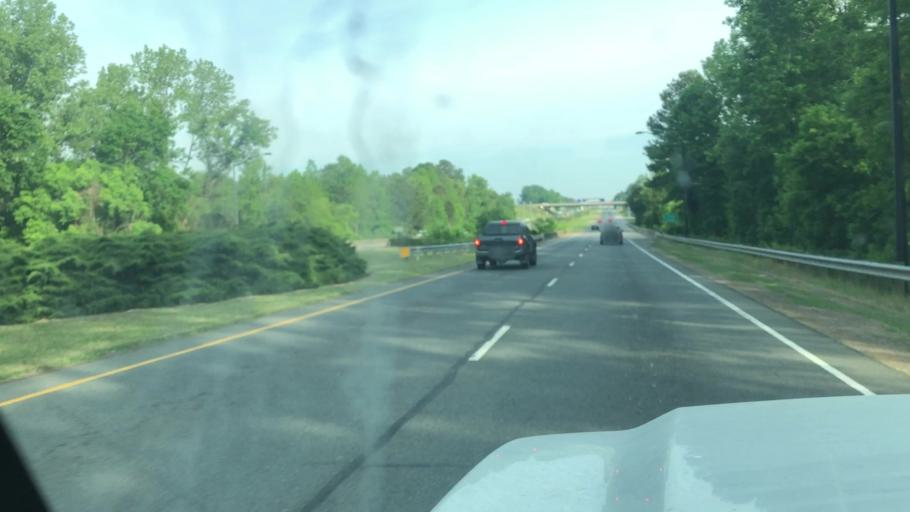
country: US
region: North Carolina
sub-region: Gaston County
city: Mount Holly
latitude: 35.3180
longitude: -80.9355
